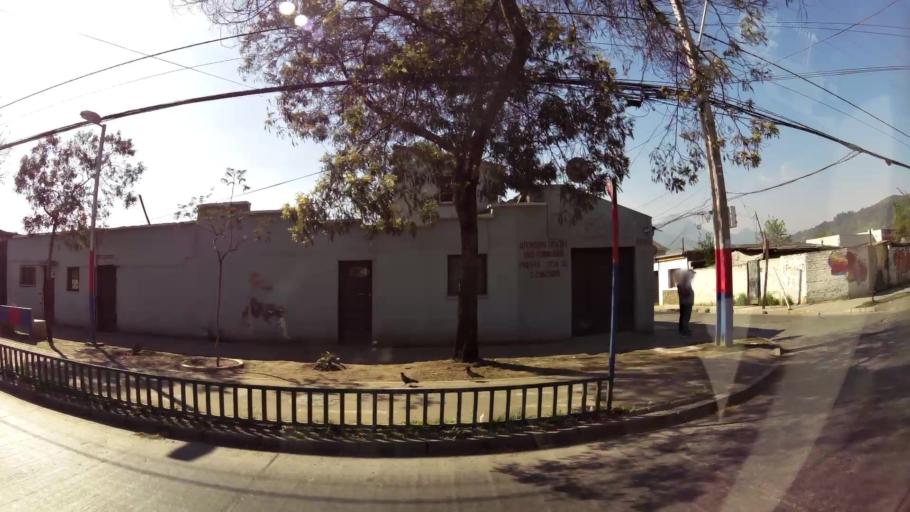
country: CL
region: Santiago Metropolitan
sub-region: Provincia de Santiago
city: Santiago
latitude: -33.4115
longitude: -70.6316
